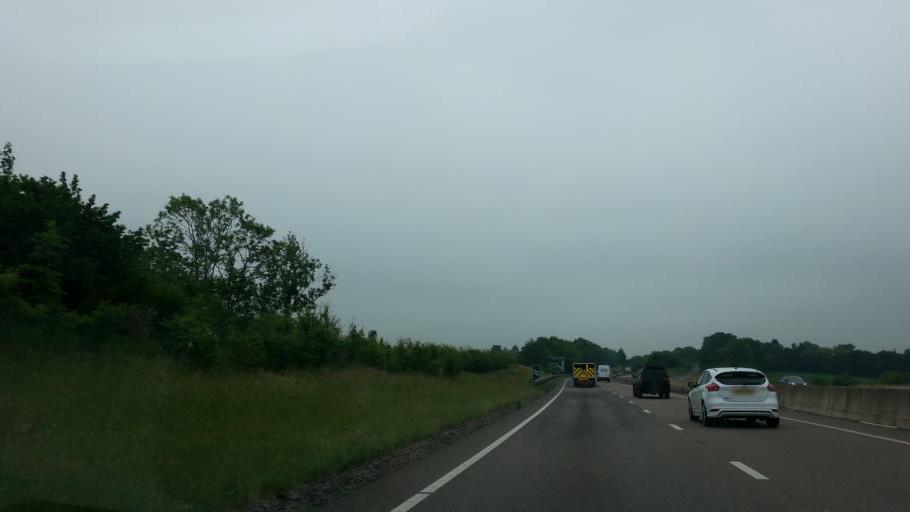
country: GB
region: England
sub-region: Nottinghamshire
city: Cotgrave
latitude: 52.8589
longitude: -1.0316
